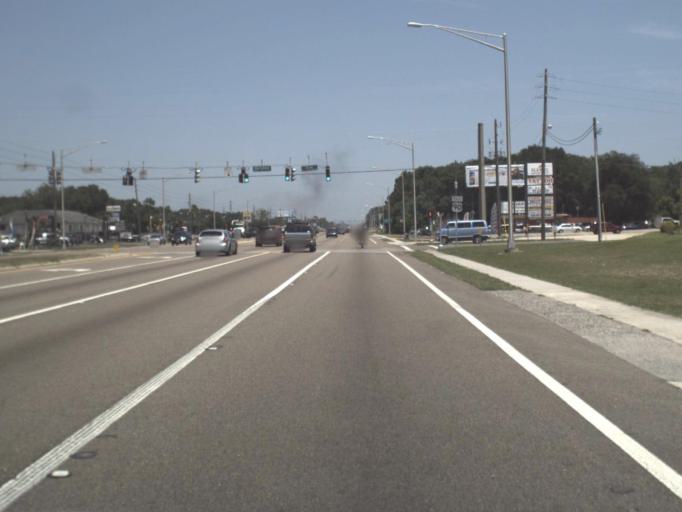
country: US
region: Florida
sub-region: Duval County
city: Jacksonville
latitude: 30.2865
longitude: -81.5557
